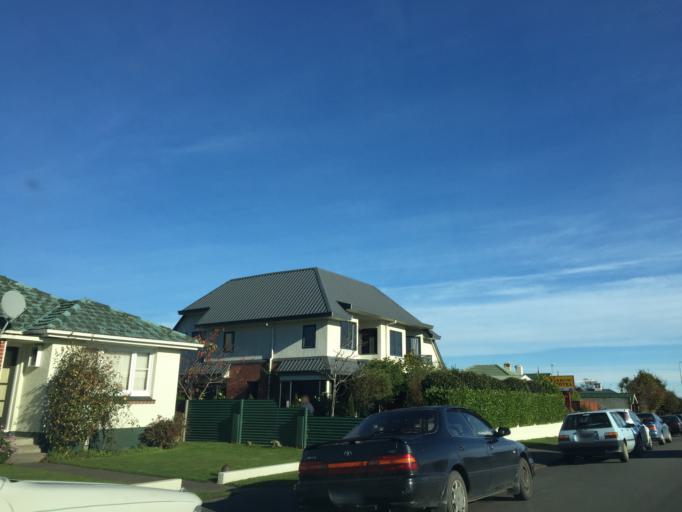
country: NZ
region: Southland
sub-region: Invercargill City
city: Invercargill
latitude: -46.4086
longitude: 168.3596
